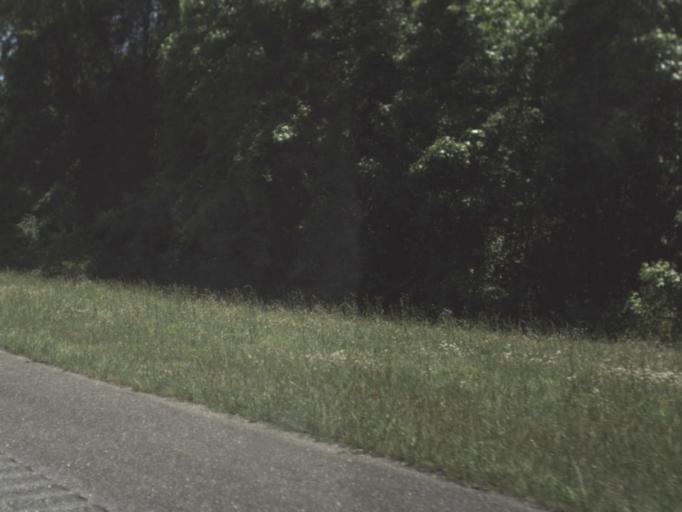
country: US
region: Florida
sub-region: Jefferson County
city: Monticello
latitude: 30.4860
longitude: -83.9519
